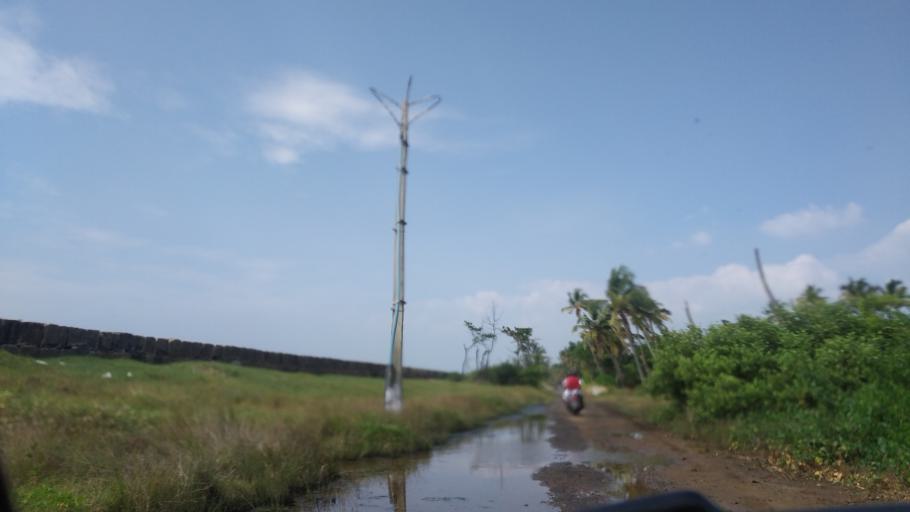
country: IN
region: Kerala
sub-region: Ernakulam
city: Elur
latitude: 10.0716
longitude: 76.1972
